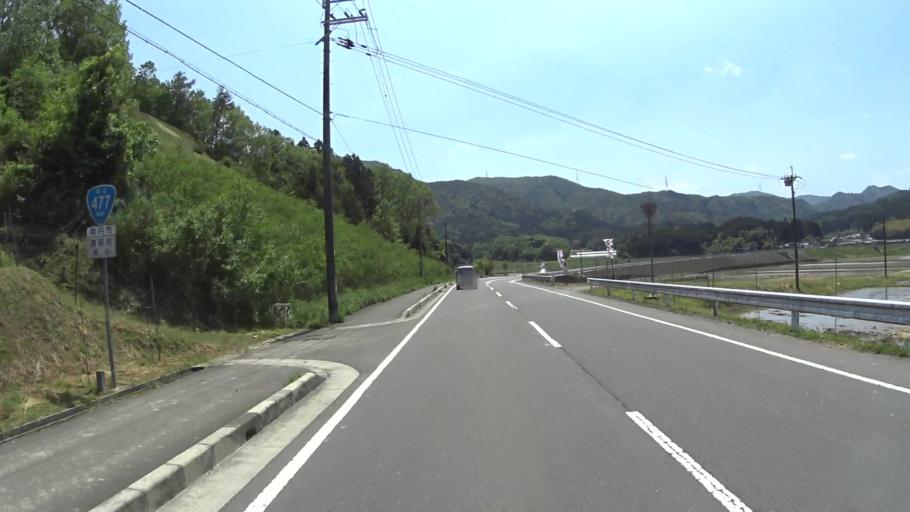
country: JP
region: Kyoto
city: Kameoka
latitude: 35.0638
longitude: 135.4591
